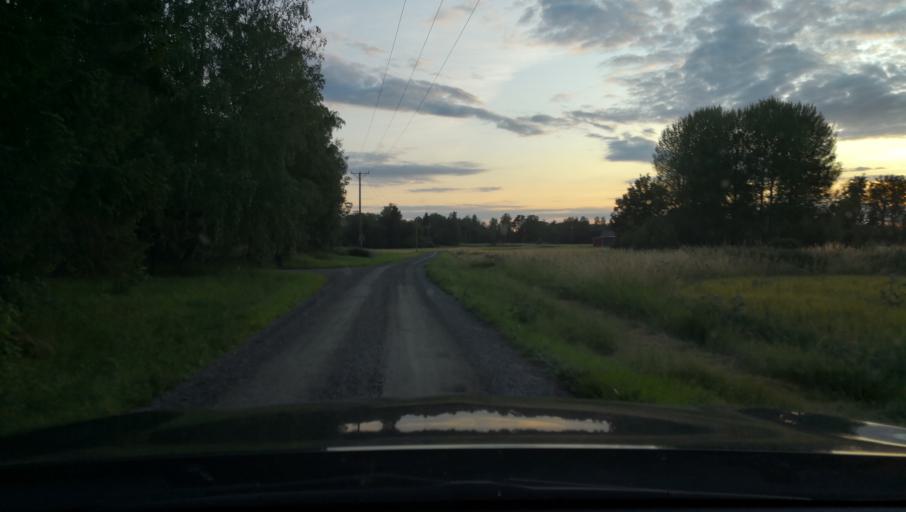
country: SE
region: Uppsala
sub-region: Osthammars Kommun
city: Bjorklinge
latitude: 60.0540
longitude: 17.6309
